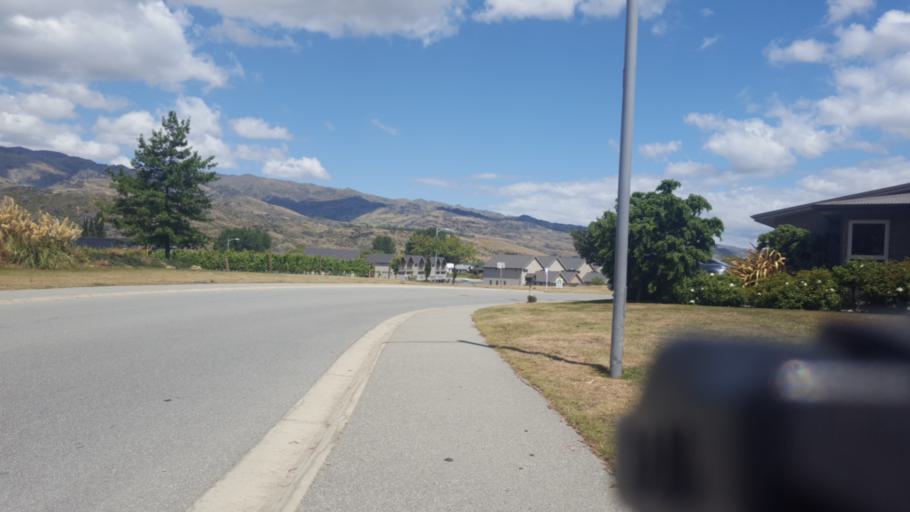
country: NZ
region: Otago
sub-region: Queenstown-Lakes District
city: Wanaka
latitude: -44.9783
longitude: 169.2360
